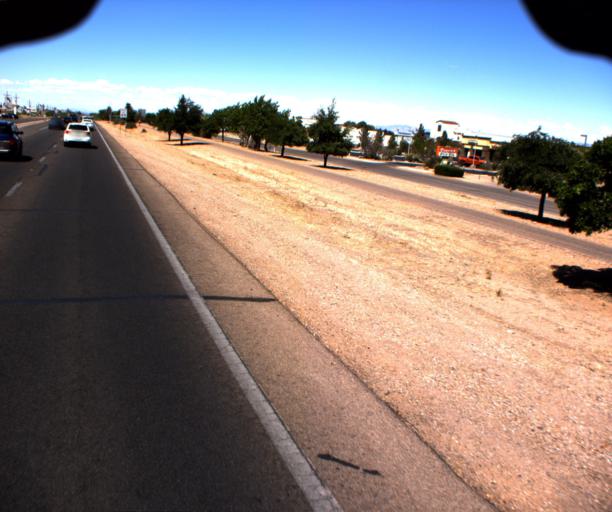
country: US
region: Arizona
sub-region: Cochise County
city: Sierra Vista
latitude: 31.5335
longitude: -110.2573
